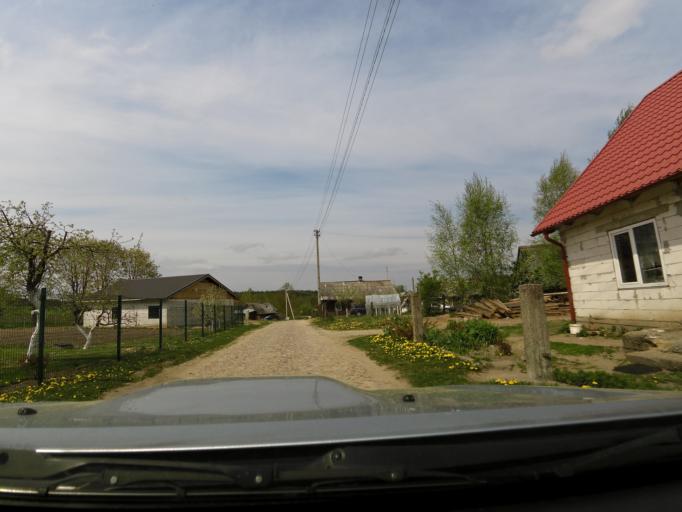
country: LT
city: Salcininkai
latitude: 54.4190
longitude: 25.3208
